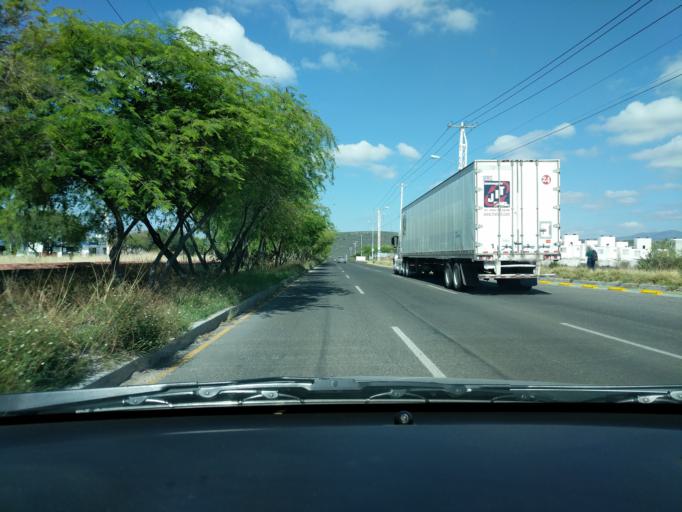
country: MX
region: Queretaro
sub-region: Queretaro
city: Patria Nueva
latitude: 20.6444
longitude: -100.4865
